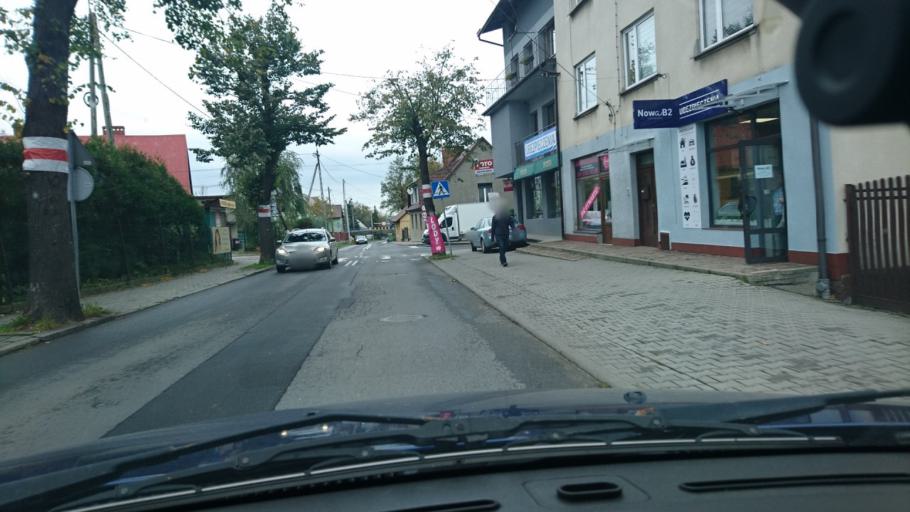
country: PL
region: Silesian Voivodeship
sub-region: Powiat bielski
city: Kozy
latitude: 49.8471
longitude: 19.1393
